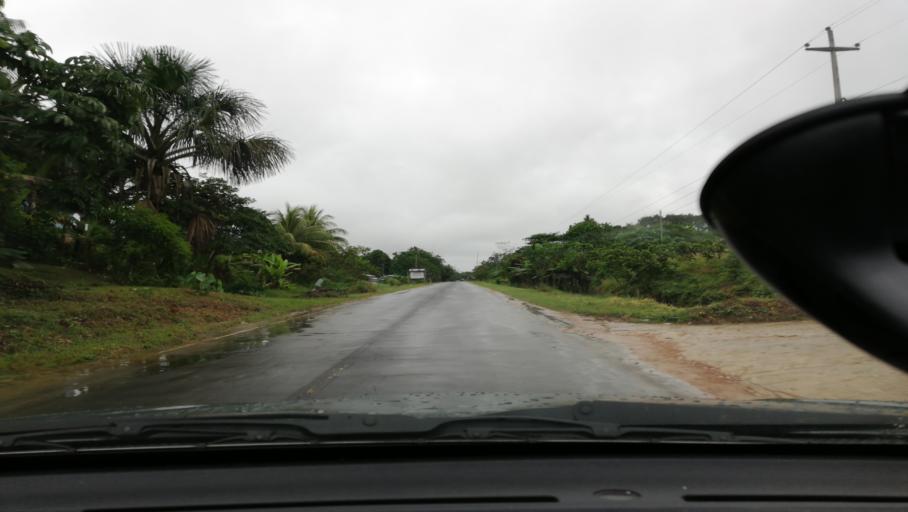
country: PE
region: Loreto
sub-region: Provincia de Maynas
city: San Juan
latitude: -4.0450
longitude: -73.4376
